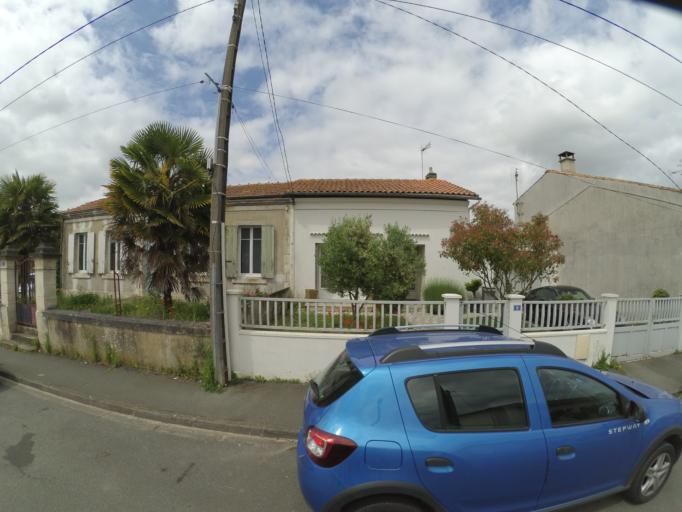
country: FR
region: Poitou-Charentes
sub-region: Departement de la Charente-Maritime
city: Rochefort
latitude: 45.9490
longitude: -0.9683
